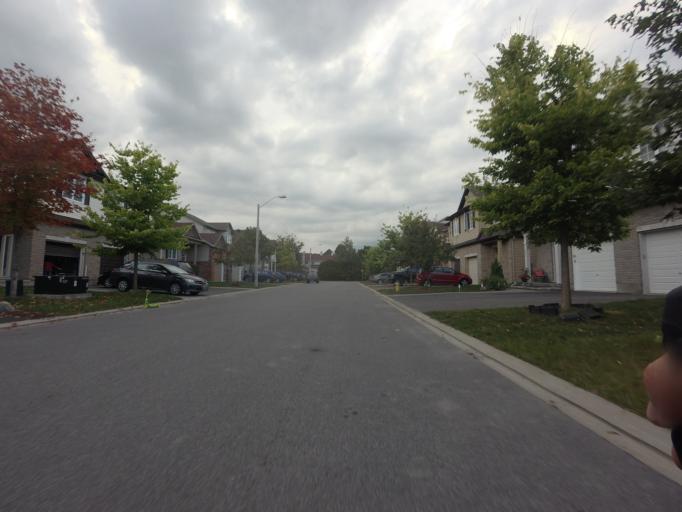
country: CA
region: Ontario
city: Bells Corners
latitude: 45.2625
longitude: -75.7623
